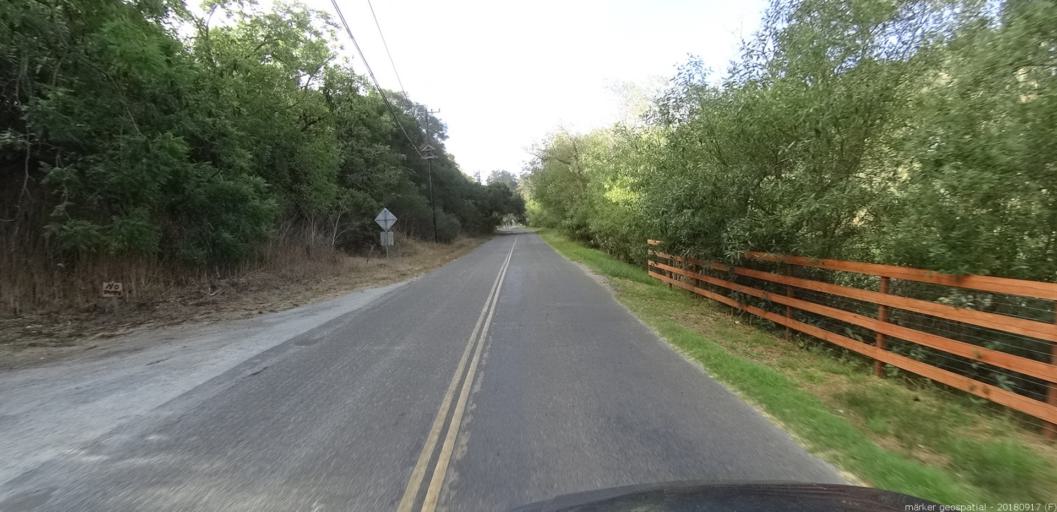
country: US
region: California
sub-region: Monterey County
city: Elkhorn
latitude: 36.8126
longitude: -121.7036
